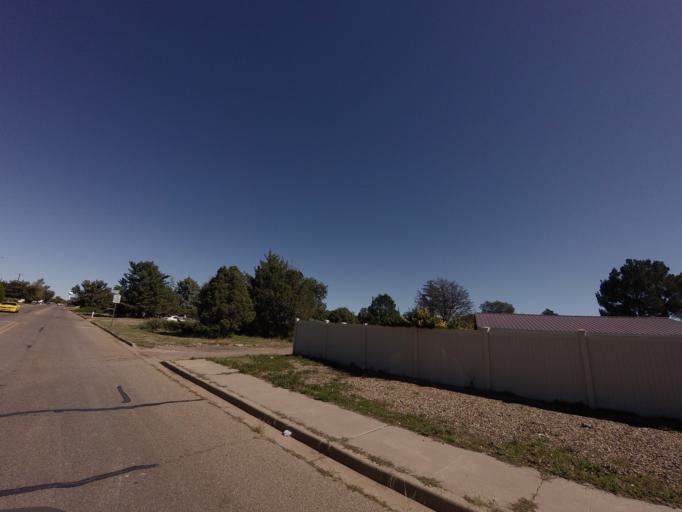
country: US
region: New Mexico
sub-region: Curry County
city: Clovis
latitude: 34.4157
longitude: -103.1877
